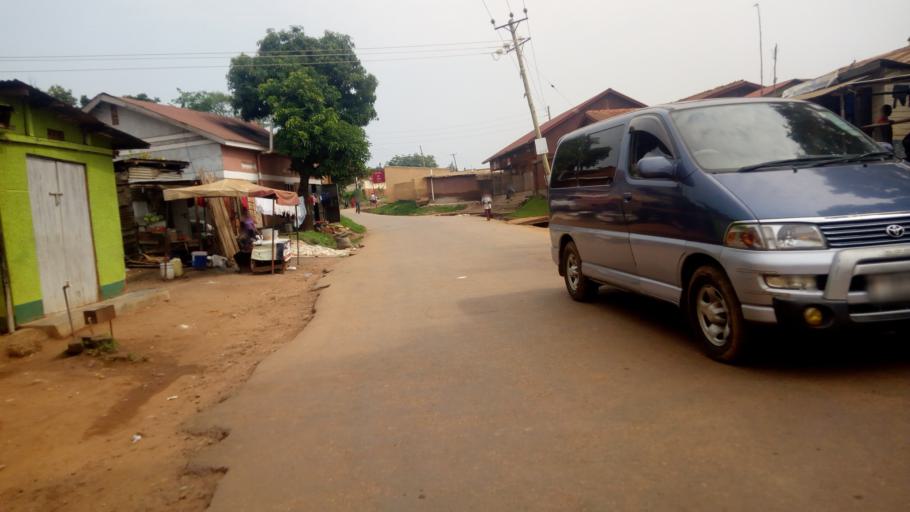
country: UG
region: Central Region
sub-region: Wakiso District
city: Kireka
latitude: 0.3031
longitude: 32.6503
